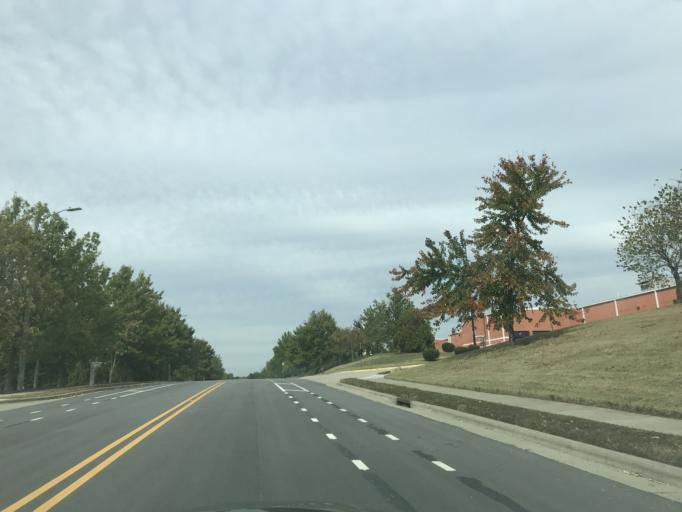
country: US
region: North Carolina
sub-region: Wake County
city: Wake Forest
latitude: 35.9426
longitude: -78.5447
